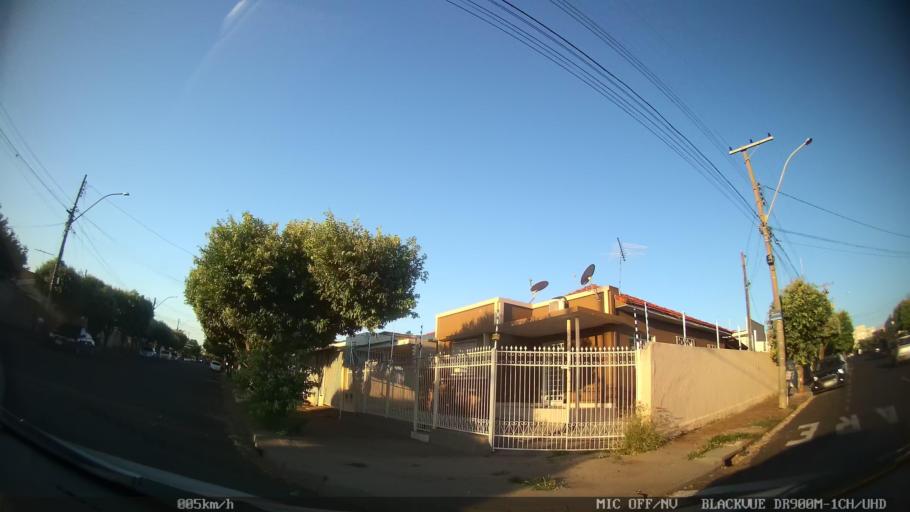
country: BR
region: Sao Paulo
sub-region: Sao Jose Do Rio Preto
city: Sao Jose do Rio Preto
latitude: -20.7974
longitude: -49.3723
